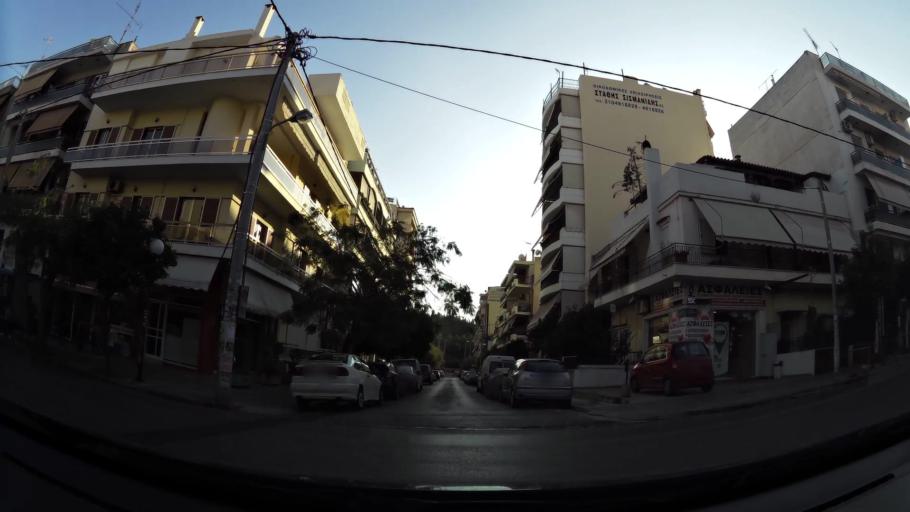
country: GR
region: Attica
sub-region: Nomos Piraios
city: Korydallos
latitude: 37.9772
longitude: 23.6381
